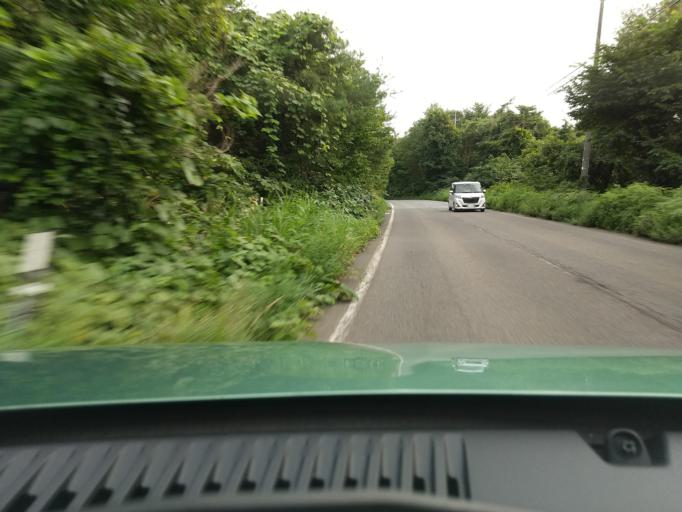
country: JP
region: Akita
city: Akita
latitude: 39.7648
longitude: 140.1329
